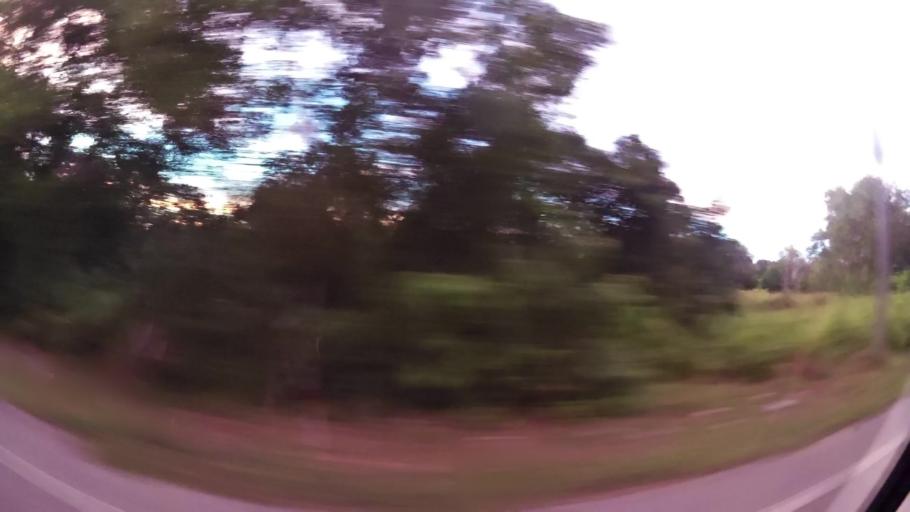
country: BN
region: Belait
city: Seria
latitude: 4.6355
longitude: 114.3919
